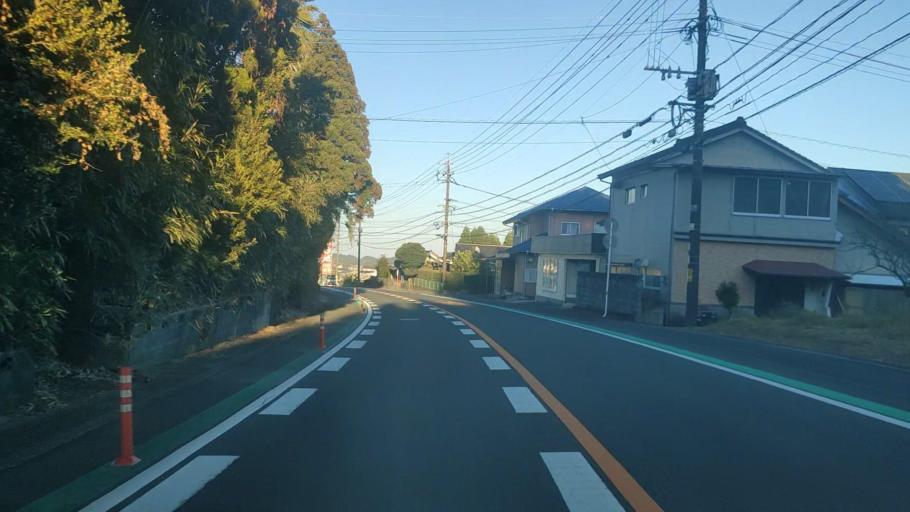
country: JP
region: Miyazaki
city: Miyazaki-shi
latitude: 31.8414
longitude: 131.3392
